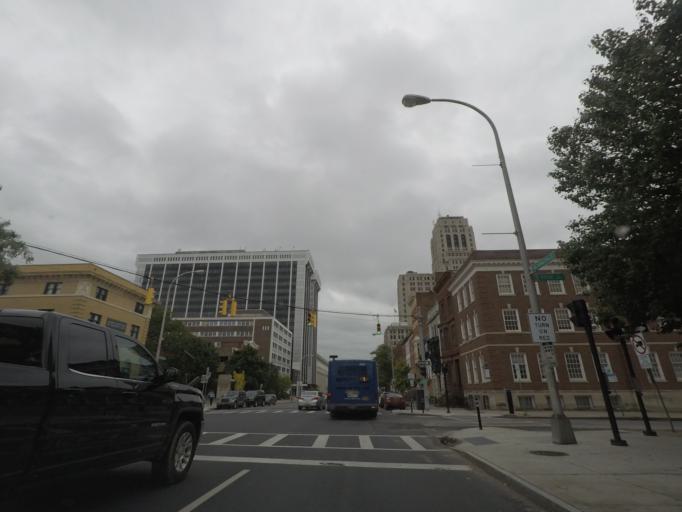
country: US
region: New York
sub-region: Albany County
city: Albany
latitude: 42.6556
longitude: -73.7614
